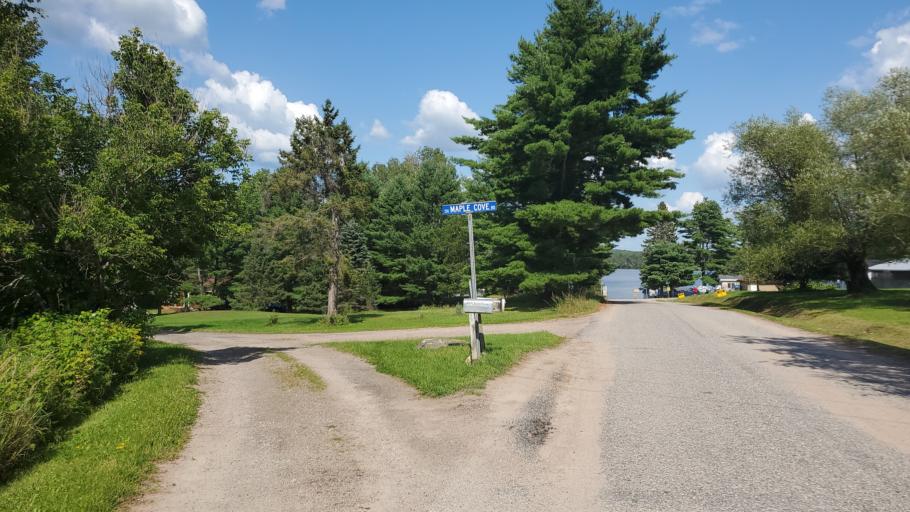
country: CA
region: Ontario
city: Powassan
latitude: 46.2186
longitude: -79.2307
